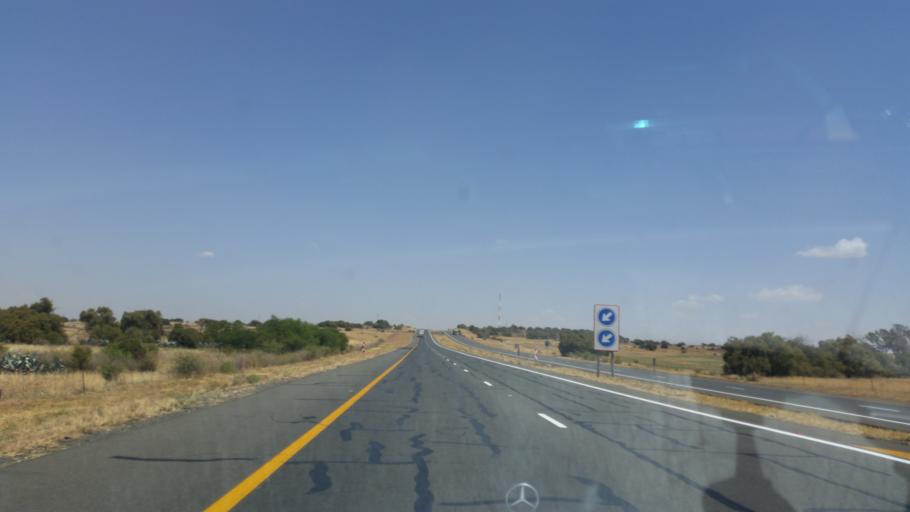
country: ZA
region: Orange Free State
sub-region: Lejweleputswa District Municipality
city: Brandfort
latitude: -28.9028
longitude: 26.4671
